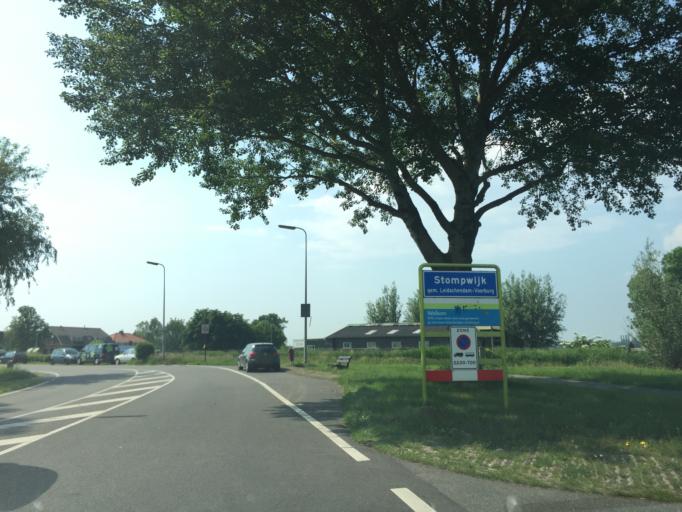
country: NL
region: South Holland
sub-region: Gemeente Voorschoten
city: Voorschoten
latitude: 52.0967
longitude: 4.4763
